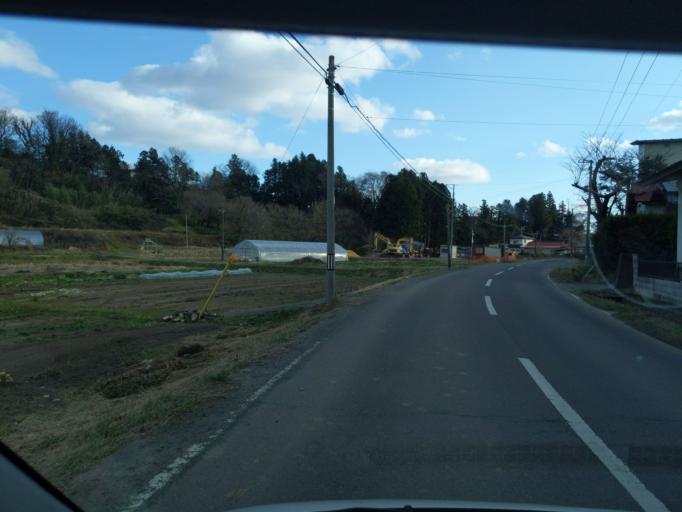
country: JP
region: Miyagi
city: Wakuya
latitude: 38.7156
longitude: 141.1463
